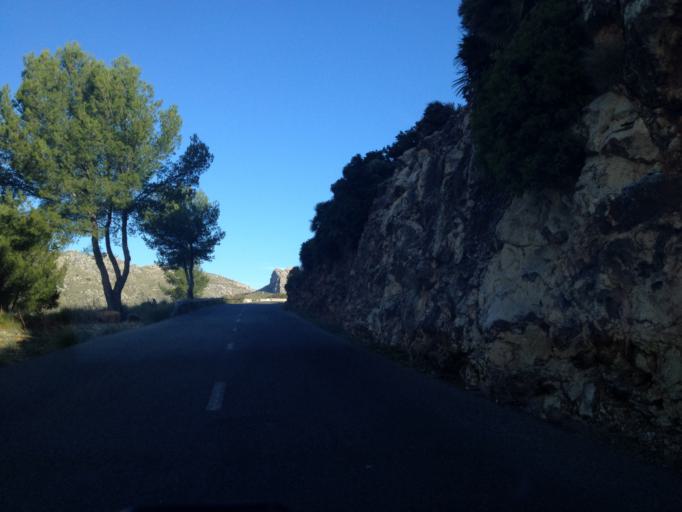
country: ES
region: Balearic Islands
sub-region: Illes Balears
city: Alcudia
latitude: 39.9116
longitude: 3.1043
